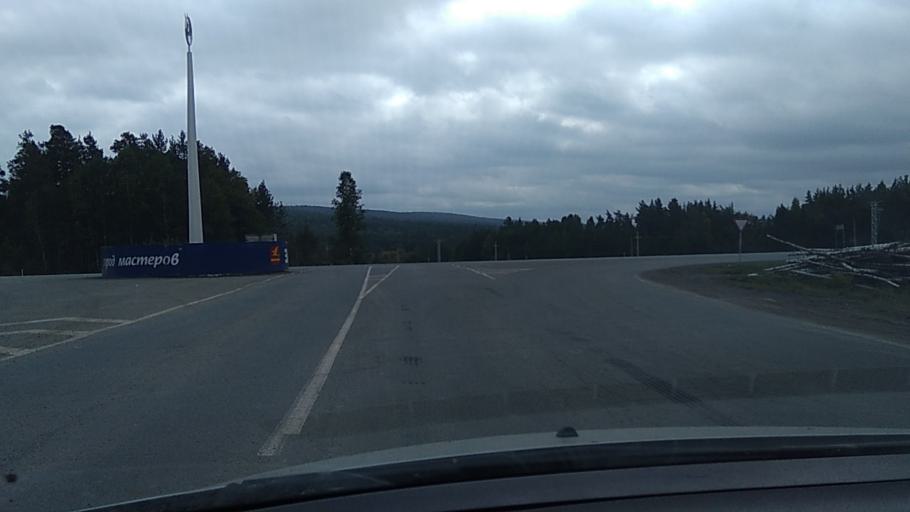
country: RU
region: Chelyabinsk
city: Zlatoust
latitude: 55.0563
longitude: 59.6968
